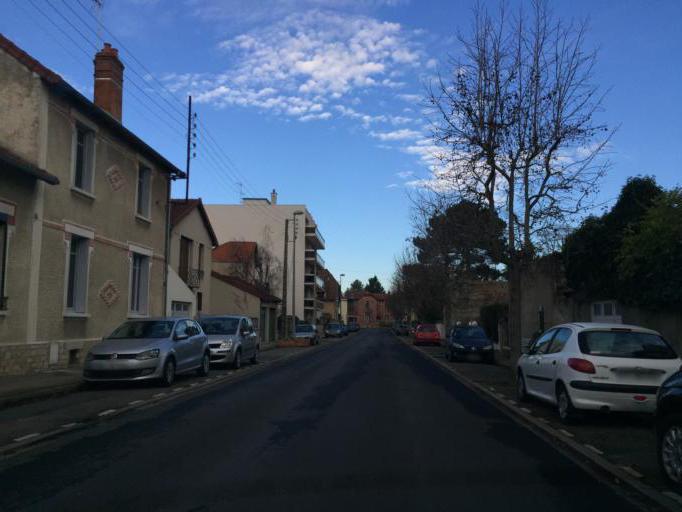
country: FR
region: Auvergne
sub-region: Departement de l'Allier
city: Moulins
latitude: 46.5709
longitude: 3.3343
